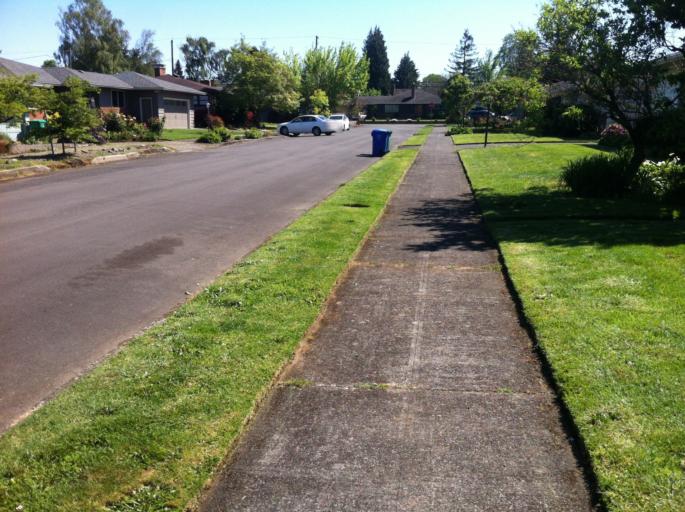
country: US
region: Oregon
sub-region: Multnomah County
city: Lents
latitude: 45.5024
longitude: -122.5928
